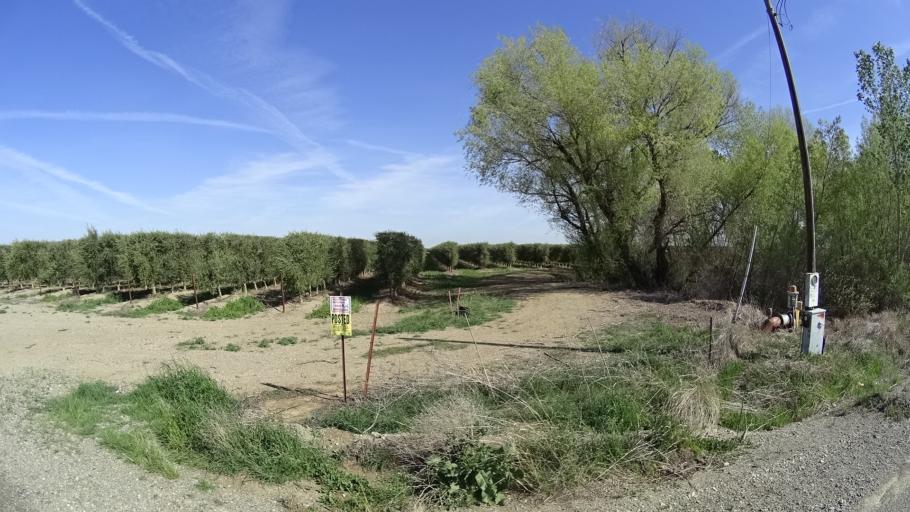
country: US
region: California
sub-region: Glenn County
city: Willows
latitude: 39.6114
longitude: -122.2339
